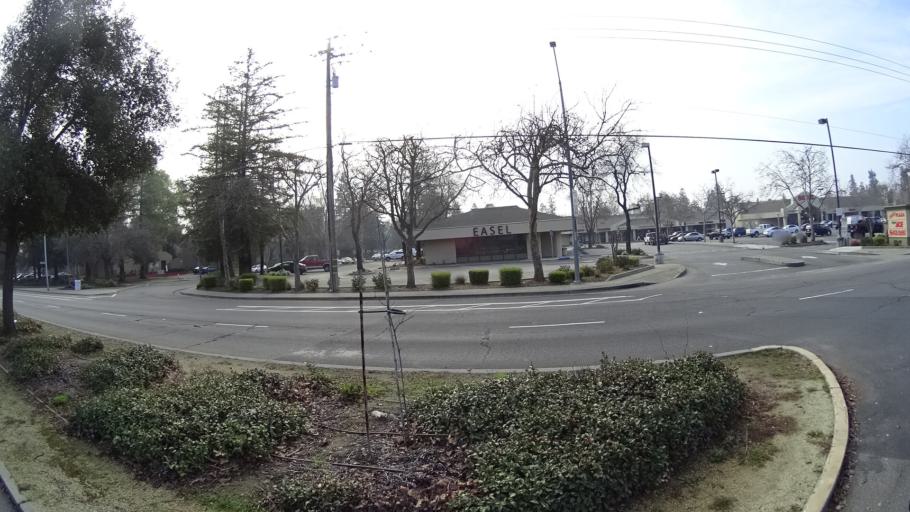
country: US
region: California
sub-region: Yolo County
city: Davis
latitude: 38.5609
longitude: -121.7568
